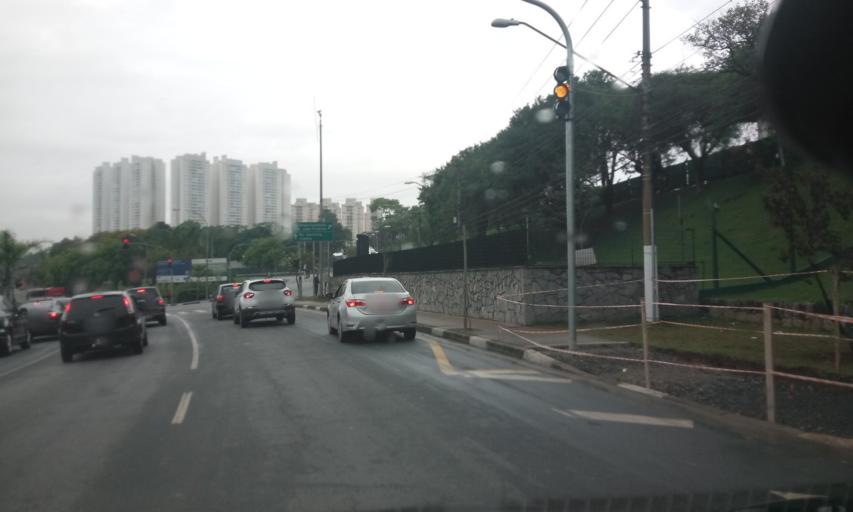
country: BR
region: Sao Paulo
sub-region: Sao Bernardo Do Campo
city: Sao Bernardo do Campo
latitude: -23.7115
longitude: -46.5661
